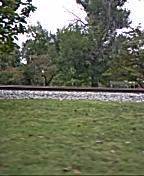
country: US
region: Kentucky
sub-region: Jefferson County
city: Anchorage
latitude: 38.2654
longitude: -85.5413
